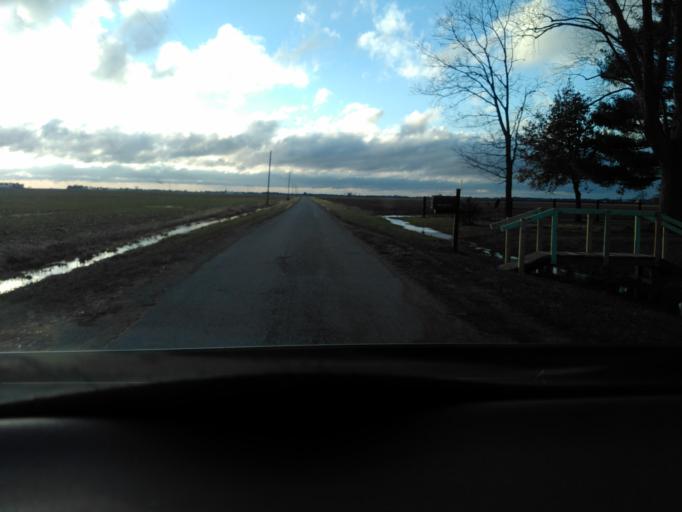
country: US
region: Illinois
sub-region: Effingham County
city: Altamont
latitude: 38.9509
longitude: -88.7055
